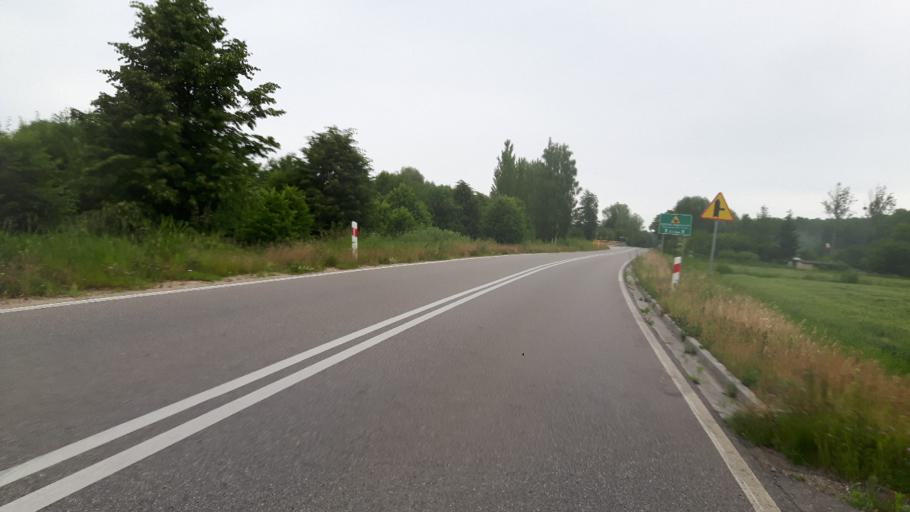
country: PL
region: Warmian-Masurian Voivodeship
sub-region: Powiat elblaski
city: Elblag
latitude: 54.2324
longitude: 19.3907
